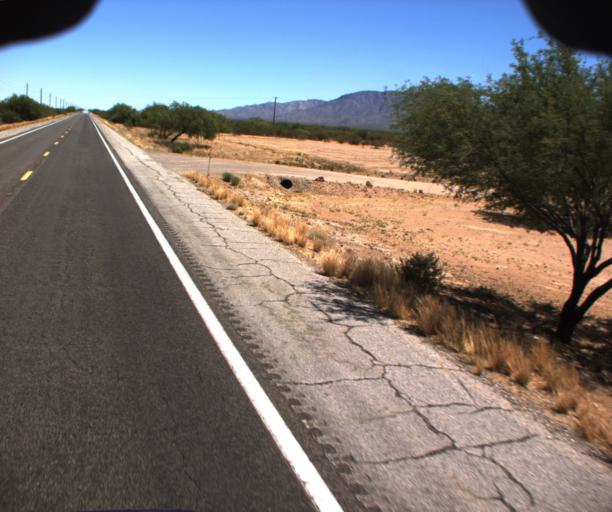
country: US
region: Arizona
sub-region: La Paz County
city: Salome
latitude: 33.8311
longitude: -113.5060
